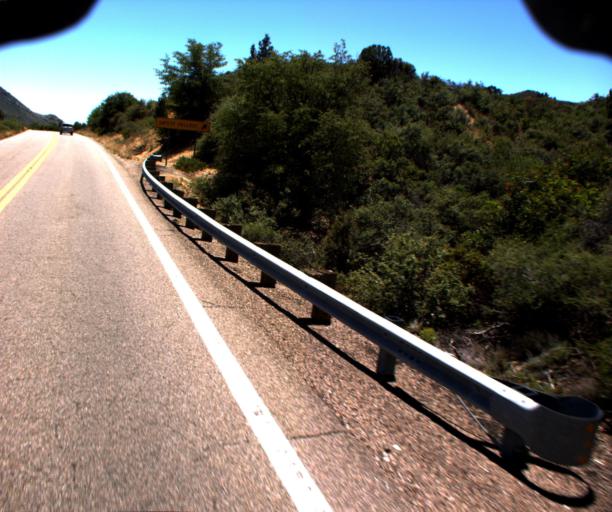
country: US
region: Arizona
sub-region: Gila County
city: Globe
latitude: 33.2472
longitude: -110.7824
